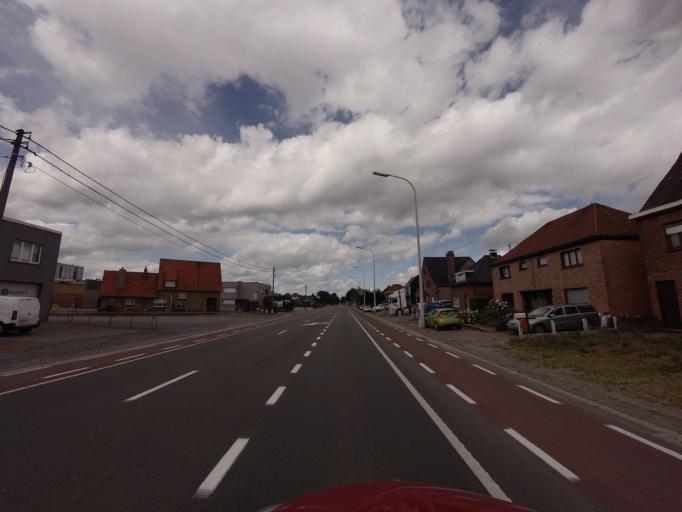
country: BE
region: Flanders
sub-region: Provincie Oost-Vlaanderen
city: Sint-Laureins
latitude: 51.2035
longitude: 3.4999
